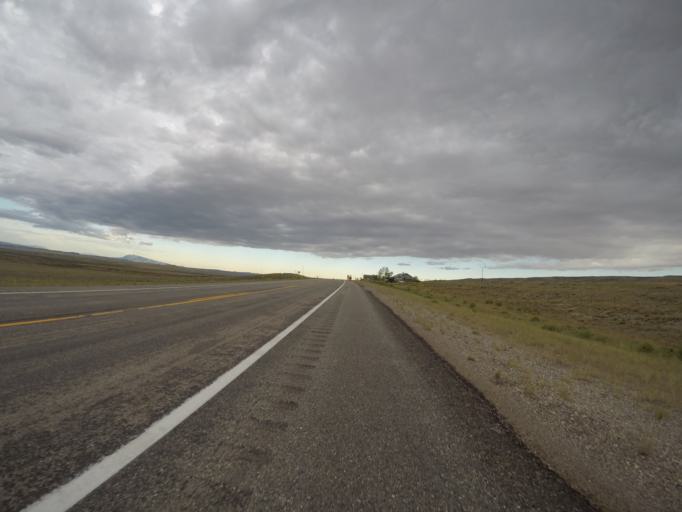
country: US
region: Wyoming
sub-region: Albany County
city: Laramie
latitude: 41.8647
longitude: -106.0710
